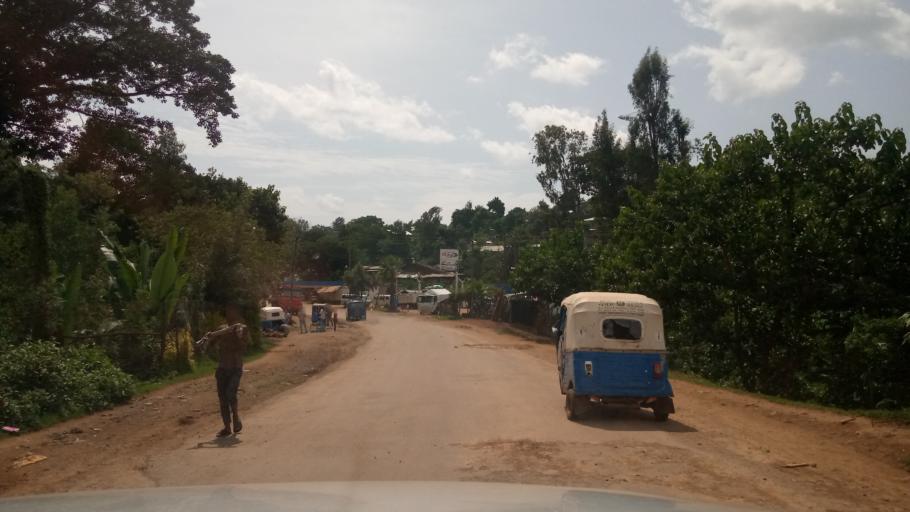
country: ET
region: Oromiya
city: Agaro
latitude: 7.8538
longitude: 36.5929
